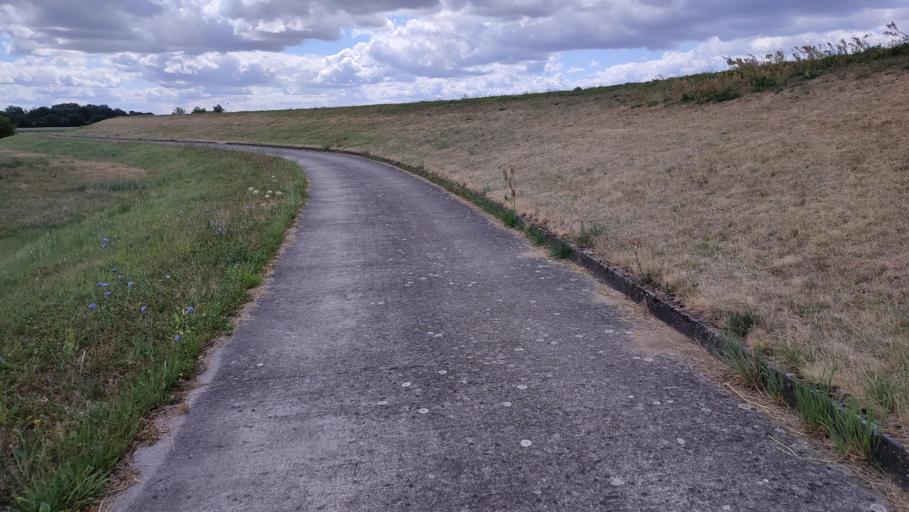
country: DE
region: Lower Saxony
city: Neu Darchau
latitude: 53.2057
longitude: 10.9702
